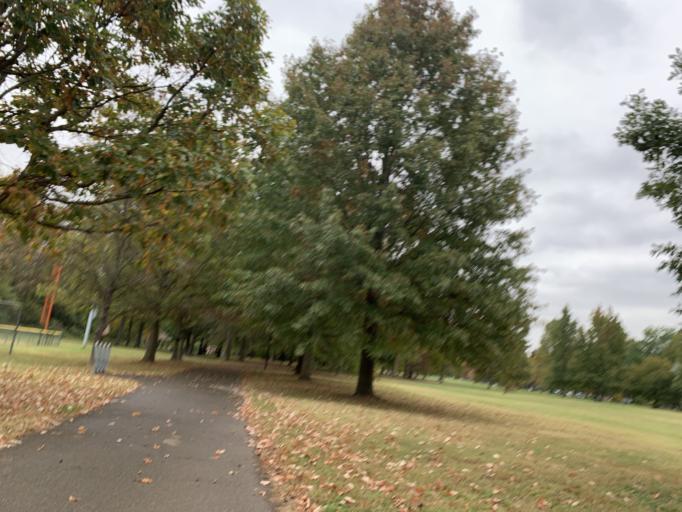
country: US
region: Indiana
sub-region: Floyd County
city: New Albany
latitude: 38.2630
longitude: -85.8277
